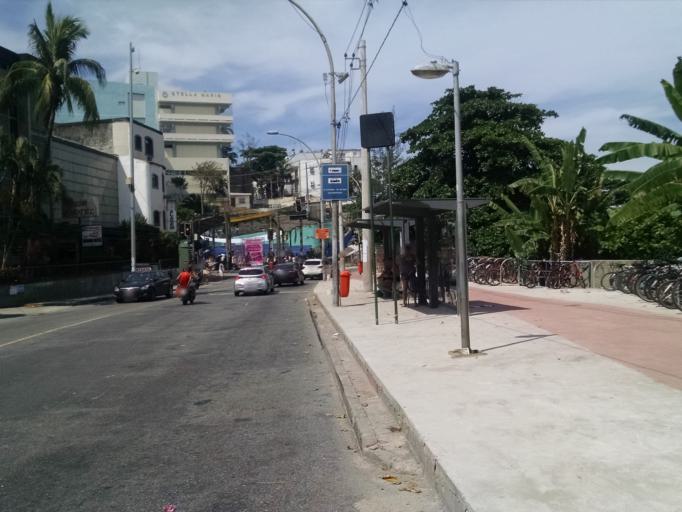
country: BR
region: Rio de Janeiro
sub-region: Rio De Janeiro
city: Rio de Janeiro
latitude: -22.9952
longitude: -43.2351
